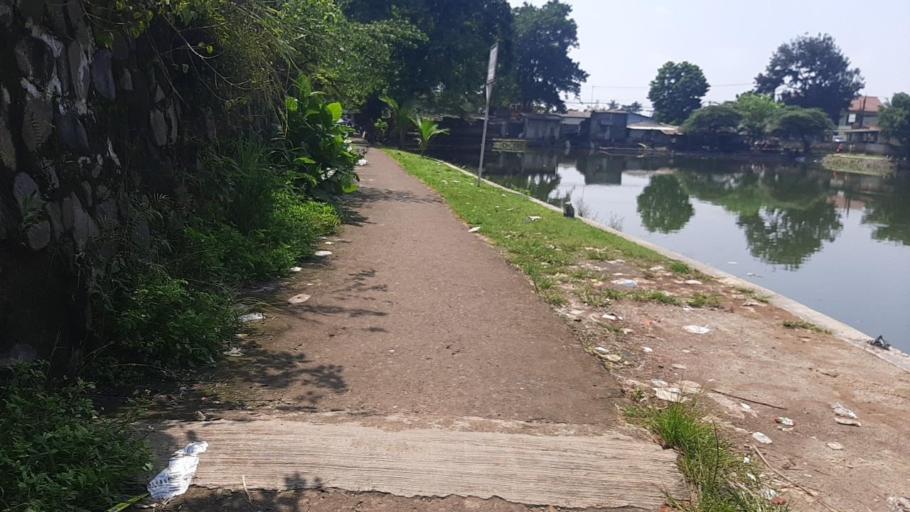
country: ID
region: West Java
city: Cileungsir
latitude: -6.4441
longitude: 106.9452
